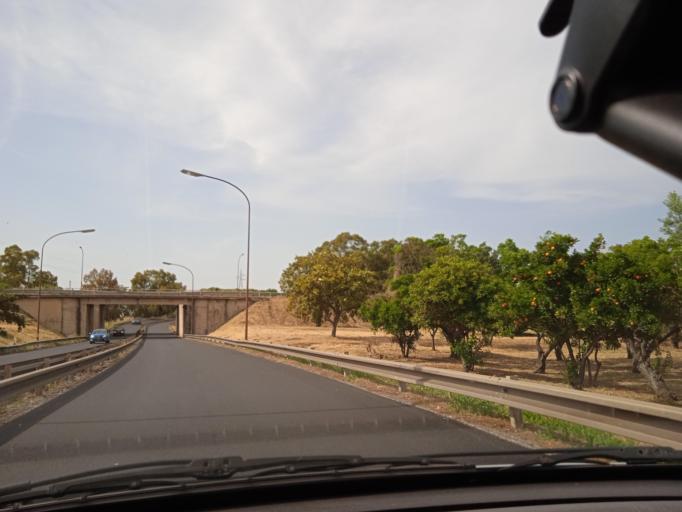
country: IT
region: Sicily
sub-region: Messina
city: San Filippo del Mela
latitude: 38.1911
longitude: 15.2745
